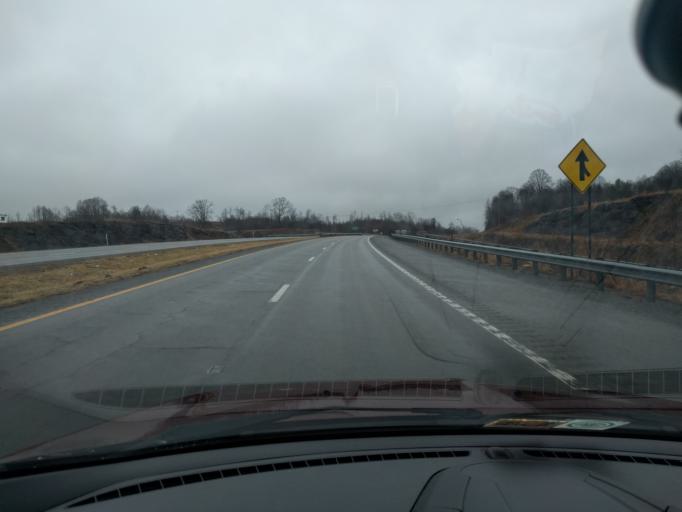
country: US
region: West Virginia
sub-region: Raleigh County
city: Sophia
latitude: 37.7209
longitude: -81.2530
